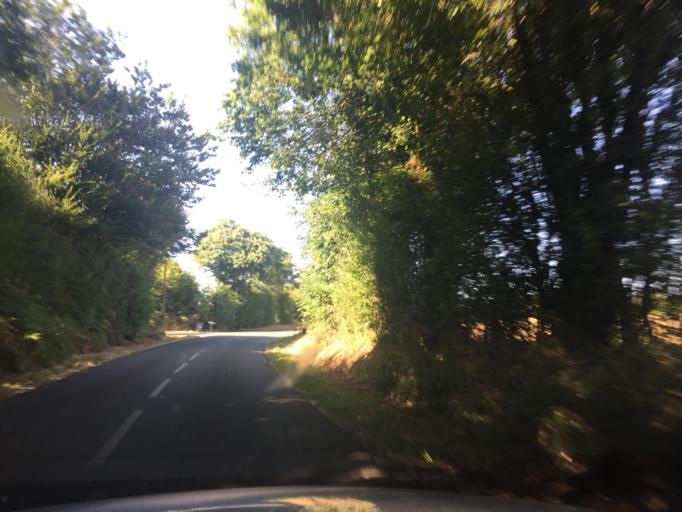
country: FR
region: Poitou-Charentes
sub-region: Departement des Deux-Sevres
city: Lezay
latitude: 46.1874
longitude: -0.0398
